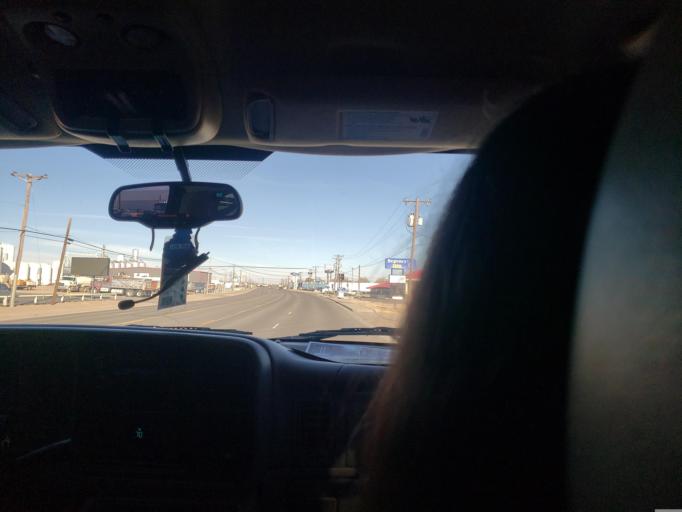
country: US
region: Texas
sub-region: Dallam County
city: Dalhart
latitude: 36.0701
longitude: -102.5125
